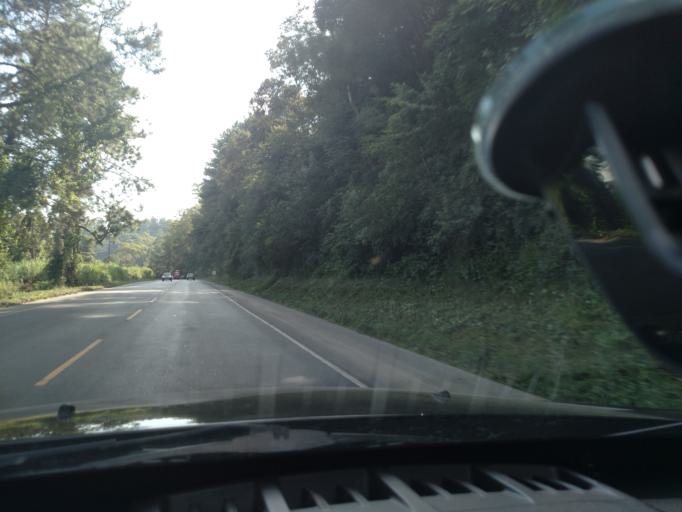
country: BR
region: Santa Catarina
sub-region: Rio Do Sul
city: Rio do Sul
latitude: -27.2356
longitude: -49.6790
